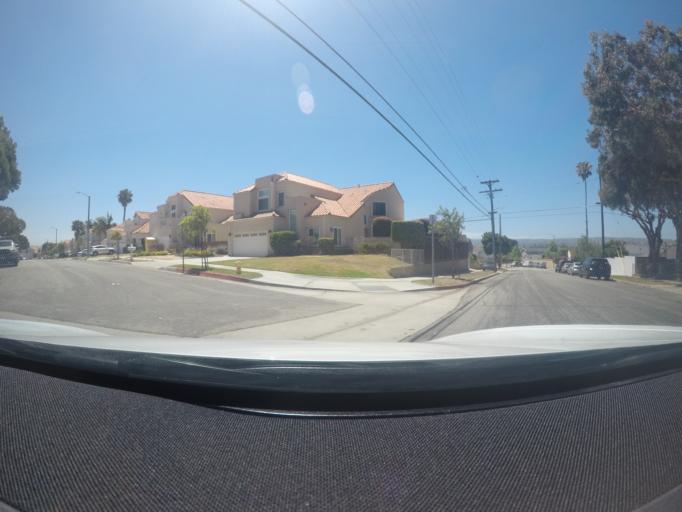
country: US
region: California
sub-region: Los Angeles County
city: Torrance
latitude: 33.8536
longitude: -118.3604
